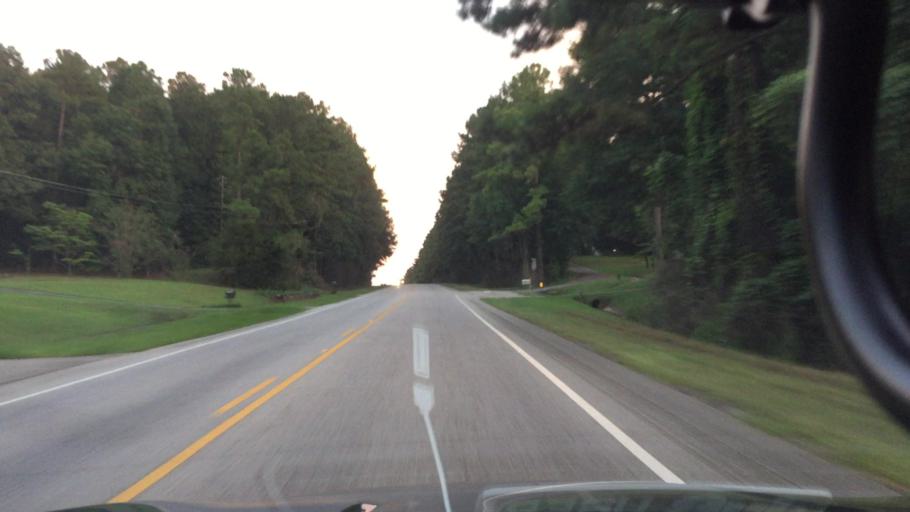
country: US
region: Alabama
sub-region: Coffee County
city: New Brockton
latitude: 31.3976
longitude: -85.8797
